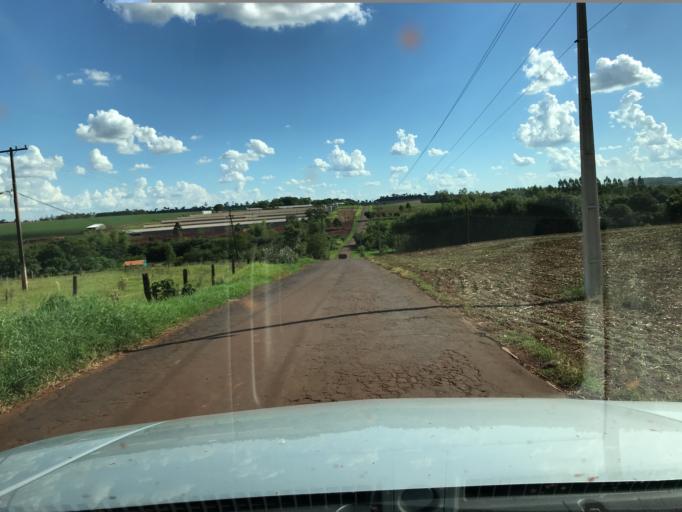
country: BR
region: Parana
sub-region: Palotina
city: Palotina
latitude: -24.2550
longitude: -53.7964
